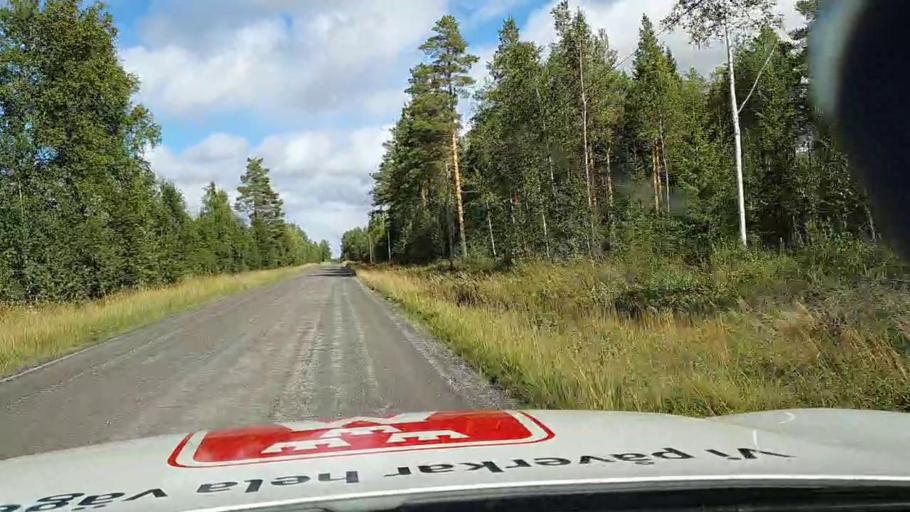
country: SE
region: Jaemtland
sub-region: Stroemsunds Kommun
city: Stroemsund
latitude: 63.6826
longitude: 15.1154
